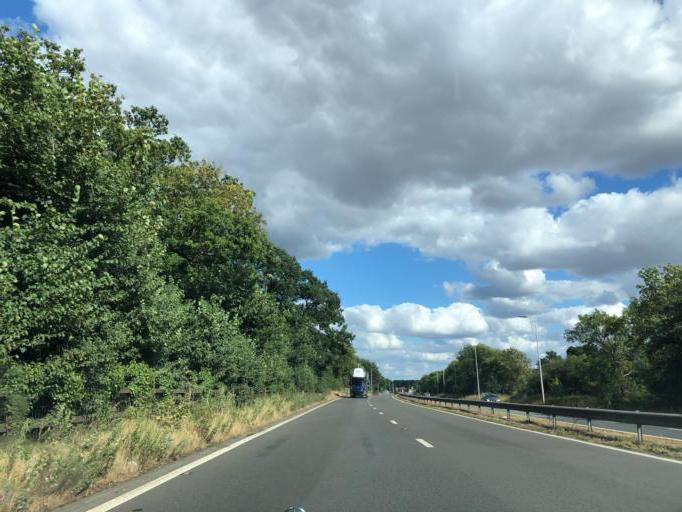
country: GB
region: England
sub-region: Warwickshire
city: Long Lawford
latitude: 52.3471
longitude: -1.3479
